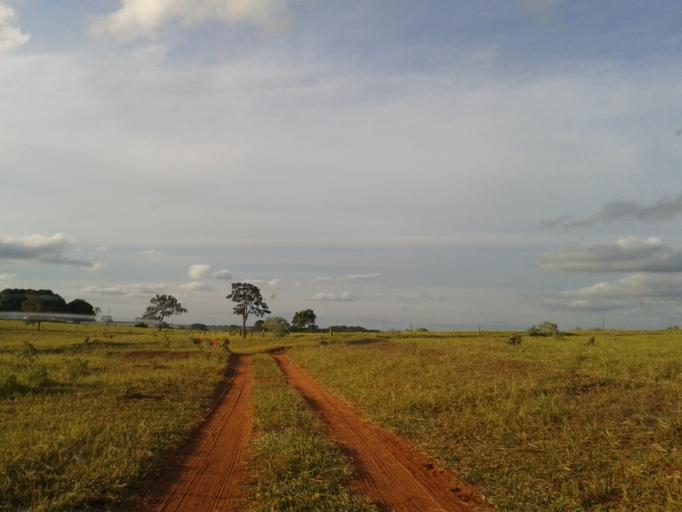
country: BR
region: Minas Gerais
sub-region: Campina Verde
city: Campina Verde
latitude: -19.4551
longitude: -49.6866
